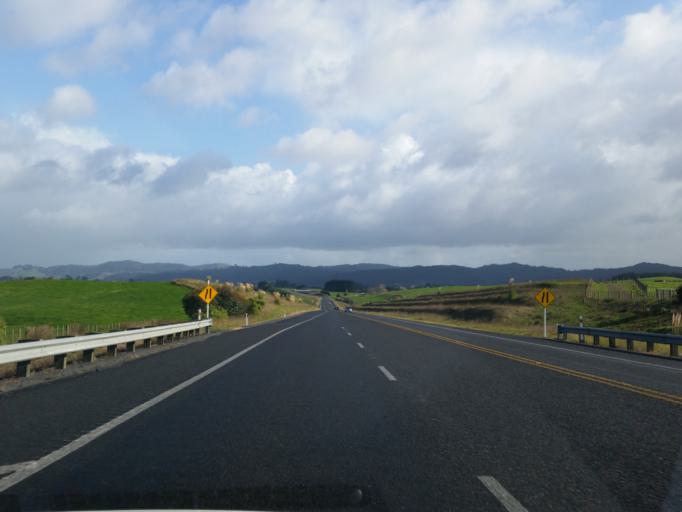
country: NZ
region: Waikato
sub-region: Waikato District
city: Te Kauwhata
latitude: -37.2267
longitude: 175.1547
